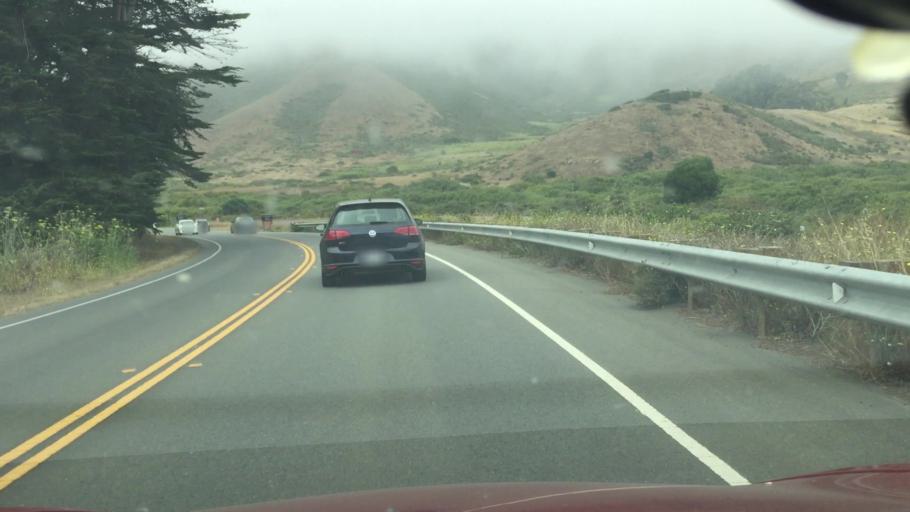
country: US
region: California
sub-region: Marin County
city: Marin City
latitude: 37.8324
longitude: -122.5170
